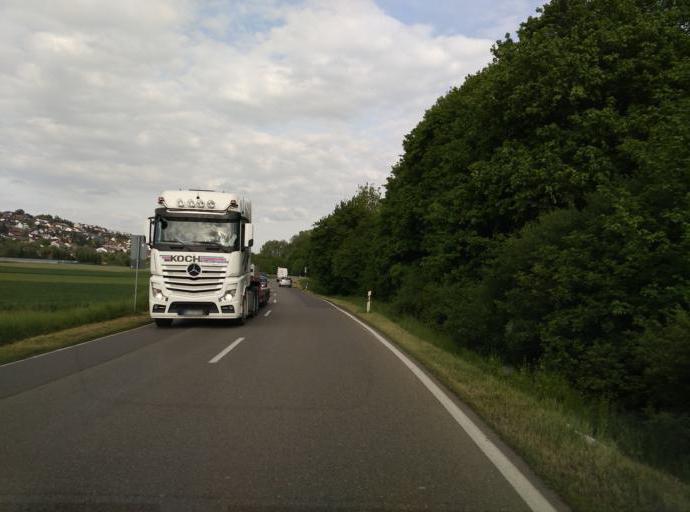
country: DE
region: Baden-Wuerttemberg
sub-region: Regierungsbezirk Stuttgart
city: Neckartailfingen
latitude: 48.6171
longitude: 9.2890
